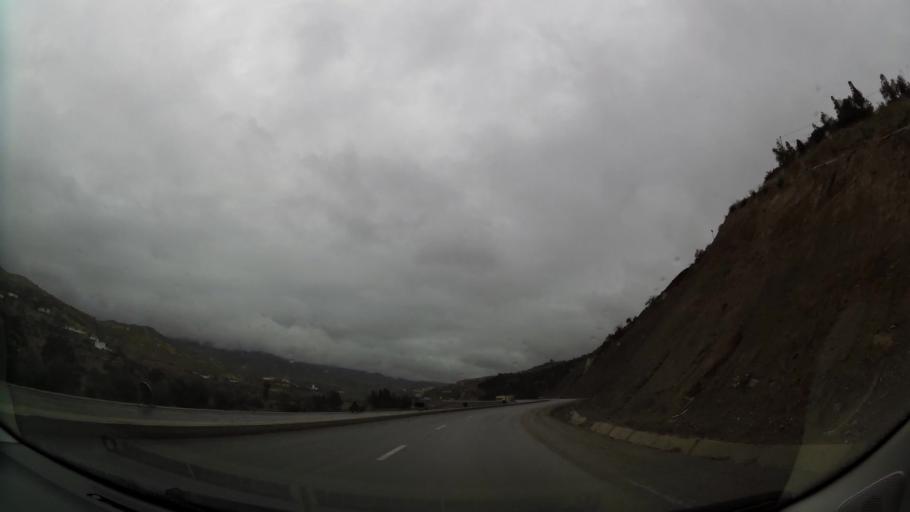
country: MA
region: Taza-Al Hoceima-Taounate
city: Imzourene
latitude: 35.0047
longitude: -3.8121
